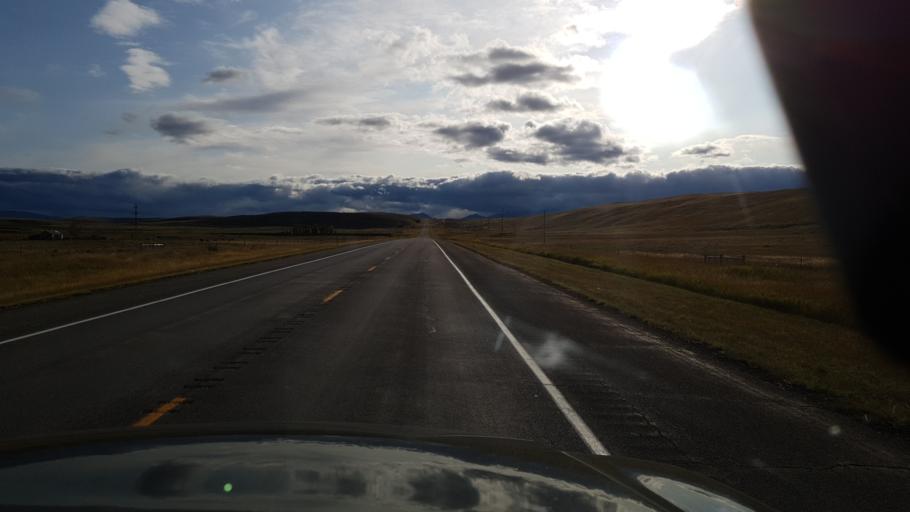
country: US
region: Montana
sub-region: Glacier County
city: South Browning
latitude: 48.5291
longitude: -113.0581
